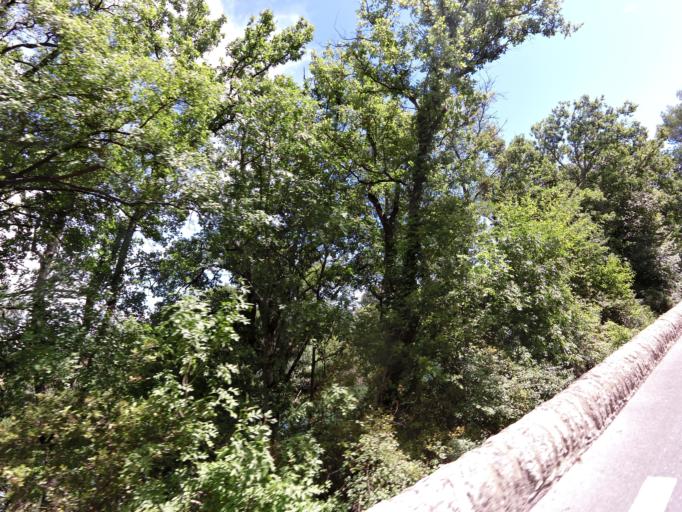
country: FR
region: Languedoc-Roussillon
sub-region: Departement du Gard
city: Sommieres
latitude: 43.7915
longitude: 4.0787
